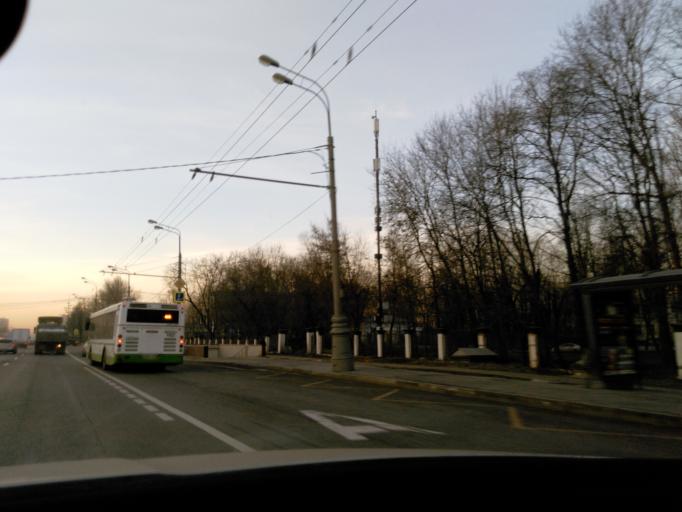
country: RU
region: Moskovskaya
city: Levoberezhnyy
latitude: 55.8497
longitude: 37.4737
